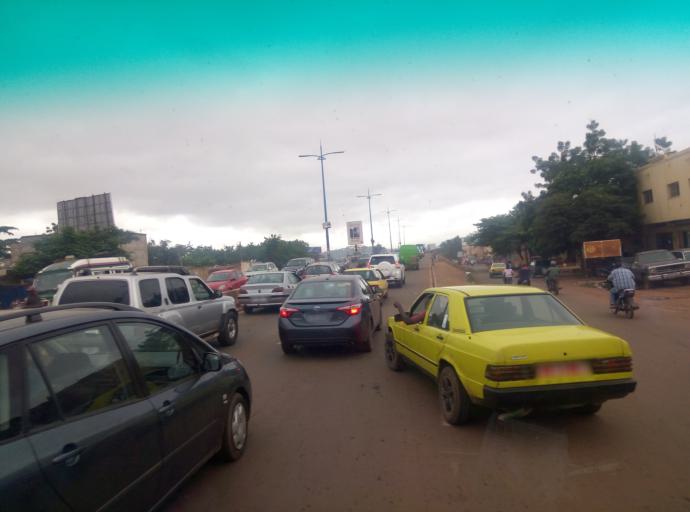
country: ML
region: Bamako
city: Bamako
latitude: 12.6121
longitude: -7.9987
